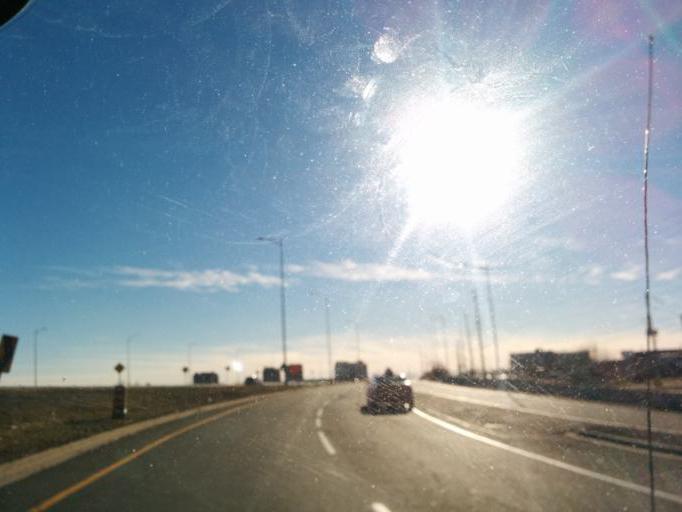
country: CA
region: Ontario
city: Etobicoke
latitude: 43.6955
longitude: -79.6068
